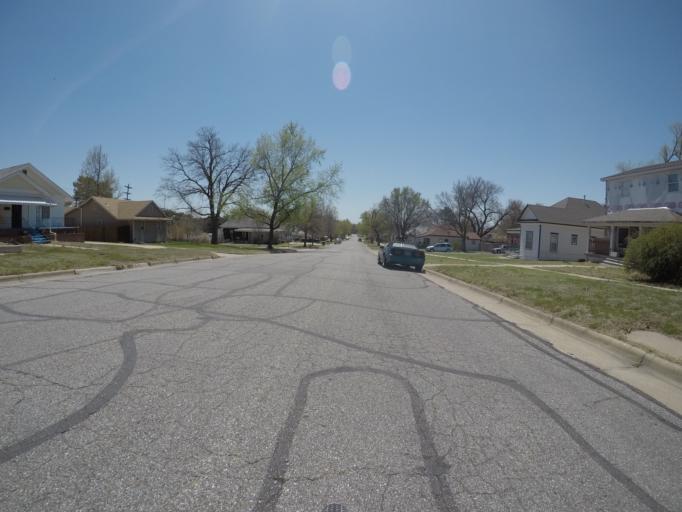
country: US
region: Kansas
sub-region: Pratt County
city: Pratt
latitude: 37.6402
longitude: -98.7356
